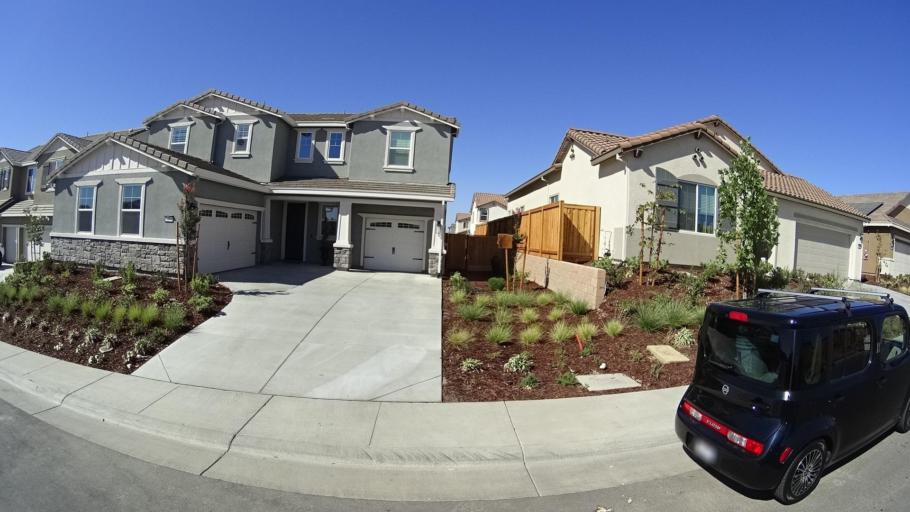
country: US
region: California
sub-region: Placer County
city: Rocklin
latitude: 38.8349
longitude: -121.2621
